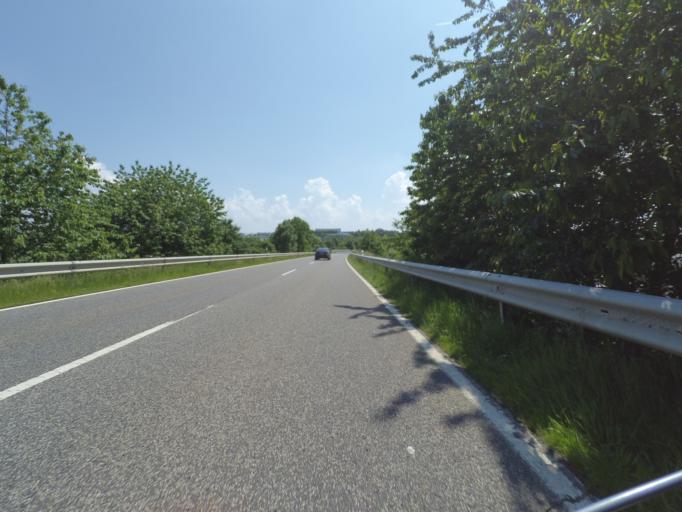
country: DE
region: Rheinland-Pfalz
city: Kaisersesch
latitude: 50.2372
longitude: 7.1454
